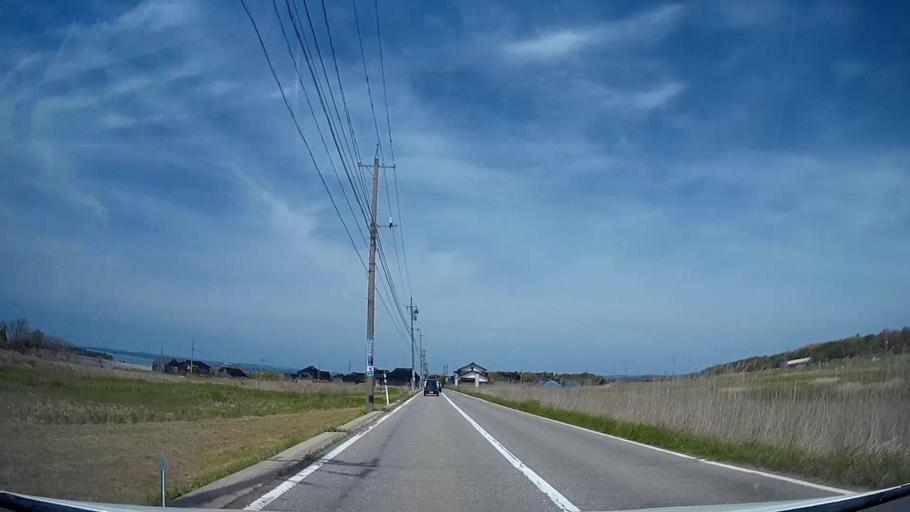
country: JP
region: Ishikawa
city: Hakui
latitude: 36.9410
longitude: 136.7613
